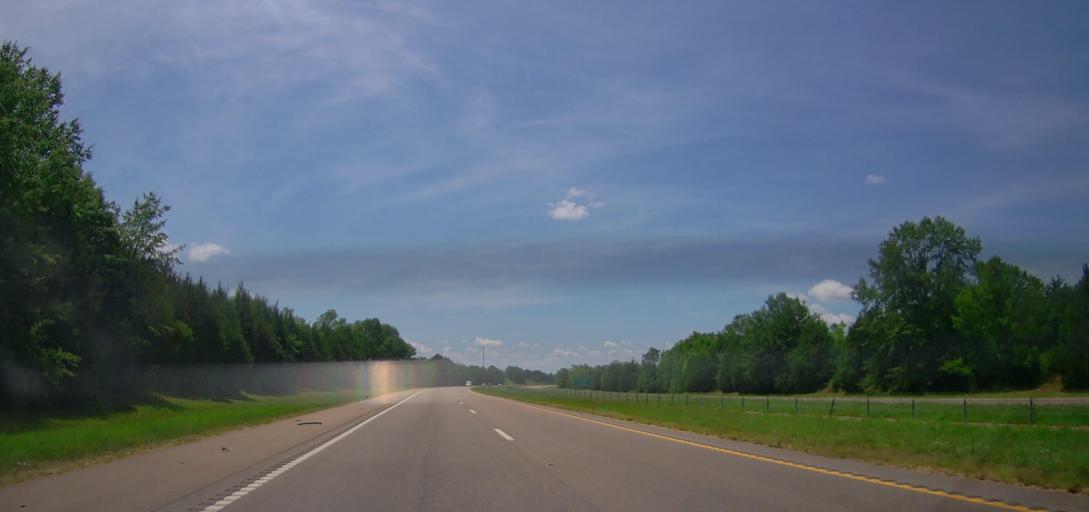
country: US
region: Mississippi
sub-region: Lee County
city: Tupelo
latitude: 34.3008
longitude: -88.7500
